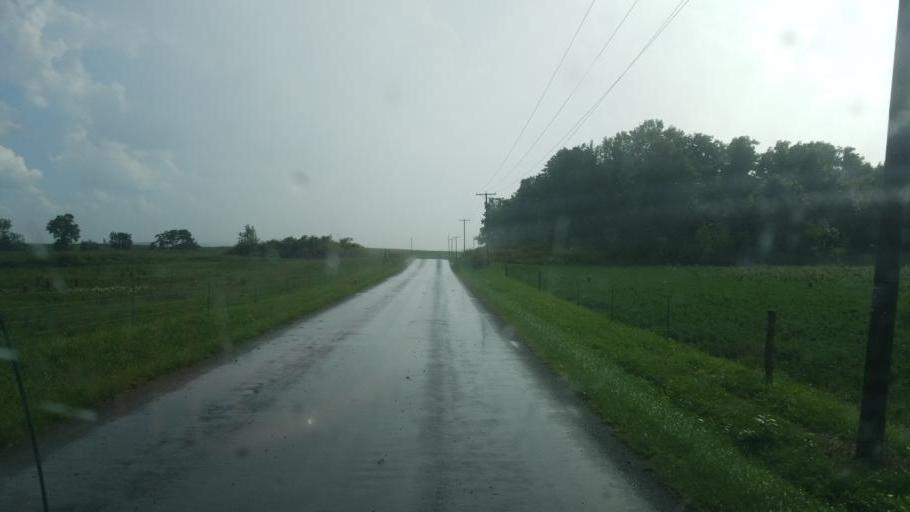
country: US
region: Ohio
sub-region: Huron County
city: Greenwich
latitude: 40.9785
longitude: -82.5590
